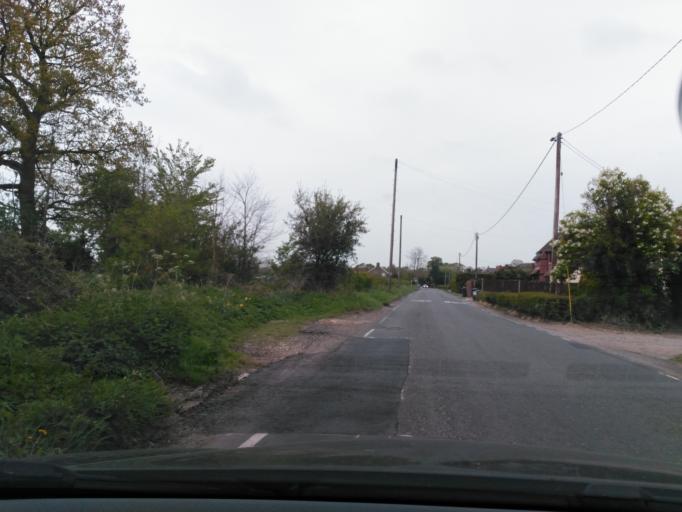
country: GB
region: England
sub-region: Hampshire
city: Tadley
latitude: 51.3222
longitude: -1.1189
